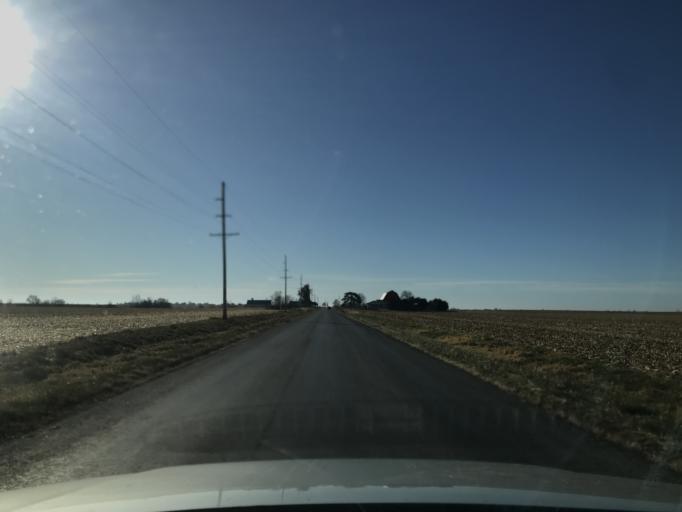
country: US
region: Illinois
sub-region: Hancock County
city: Carthage
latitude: 40.4948
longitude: -91.1778
